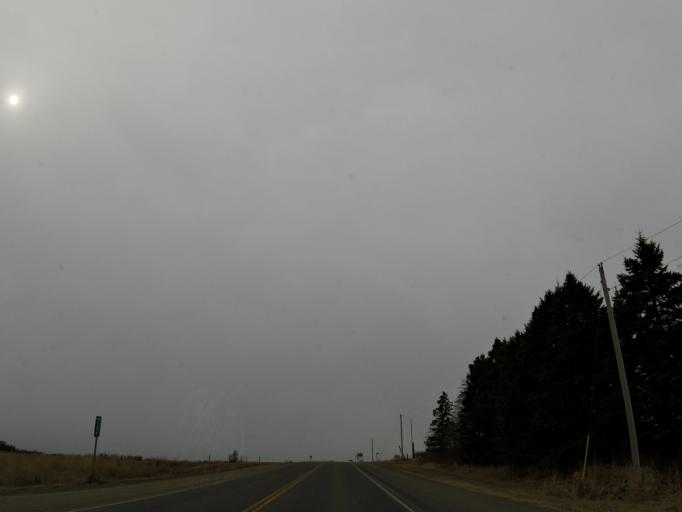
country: US
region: Minnesota
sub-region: Le Sueur County
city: Le Sueur
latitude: 44.5431
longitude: -93.8631
